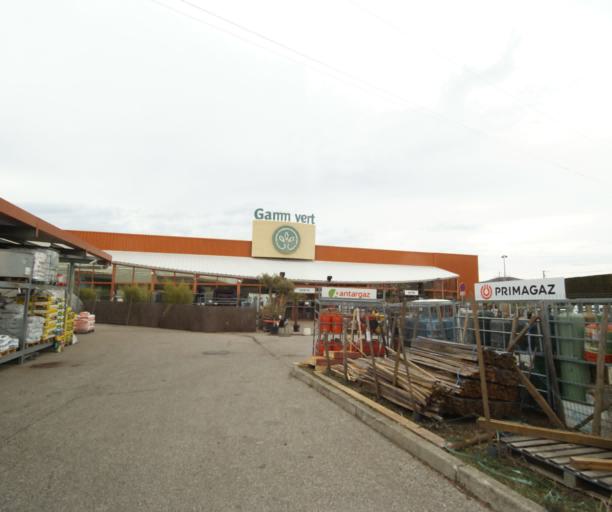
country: FR
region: Rhone-Alpes
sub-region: Departement de l'Ardeche
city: Davezieux
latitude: 45.2590
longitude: 4.7018
